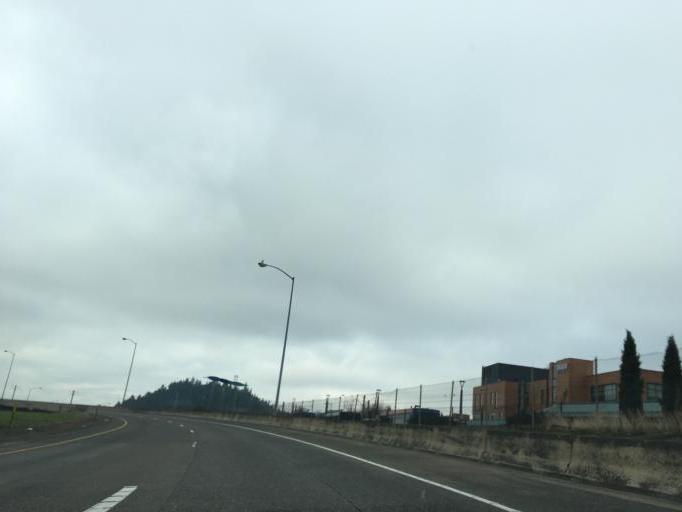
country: US
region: Oregon
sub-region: Multnomah County
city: Lents
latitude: 45.5298
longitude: -122.5639
